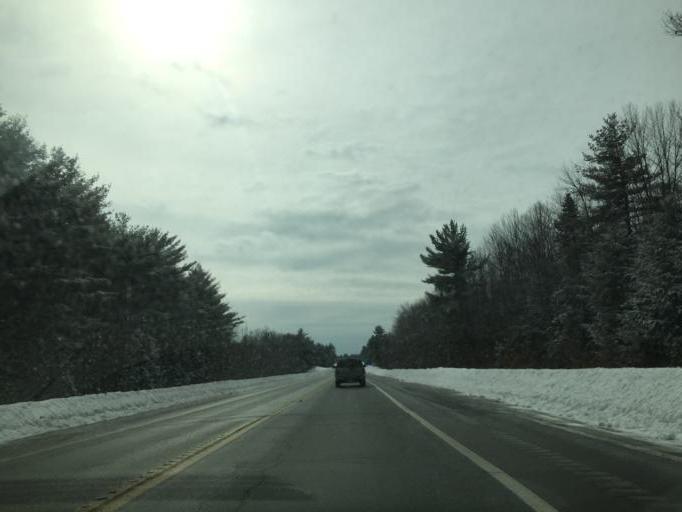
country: US
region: New Hampshire
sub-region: Strafford County
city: Rochester
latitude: 43.3455
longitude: -70.9849
